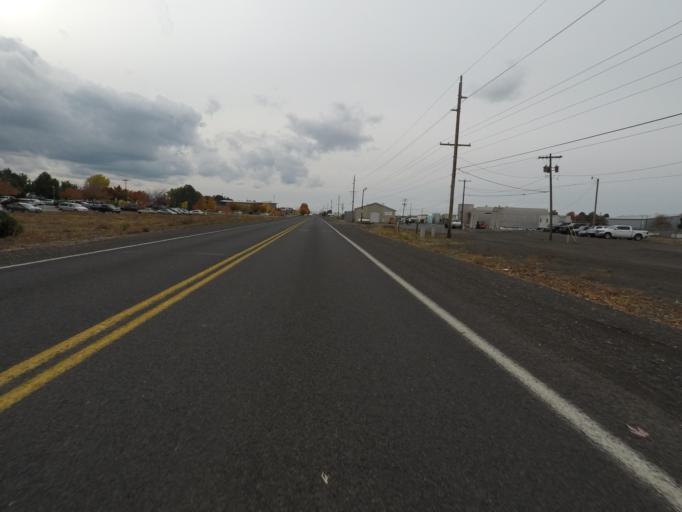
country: US
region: Washington
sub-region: Walla Walla County
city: Walla Walla East
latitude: 46.0818
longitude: -118.2764
